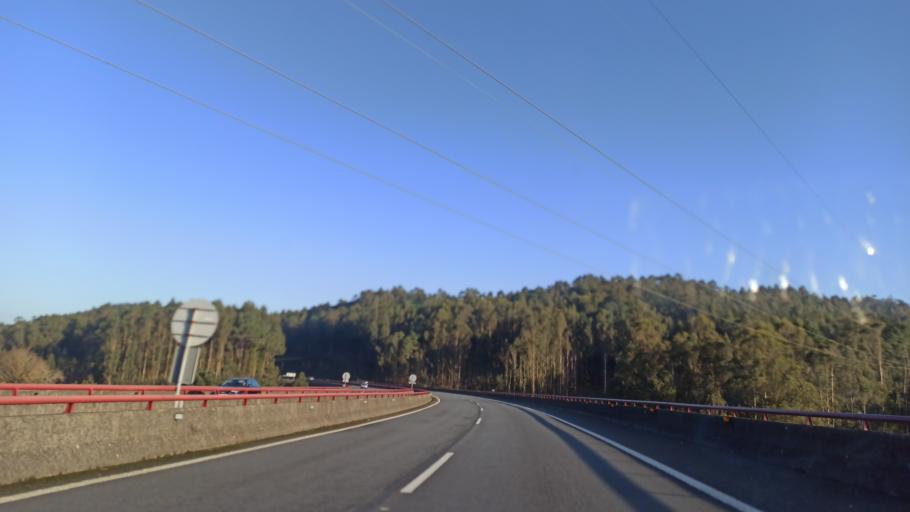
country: ES
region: Galicia
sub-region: Provincia da Coruna
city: Mino
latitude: 43.3339
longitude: -8.1978
